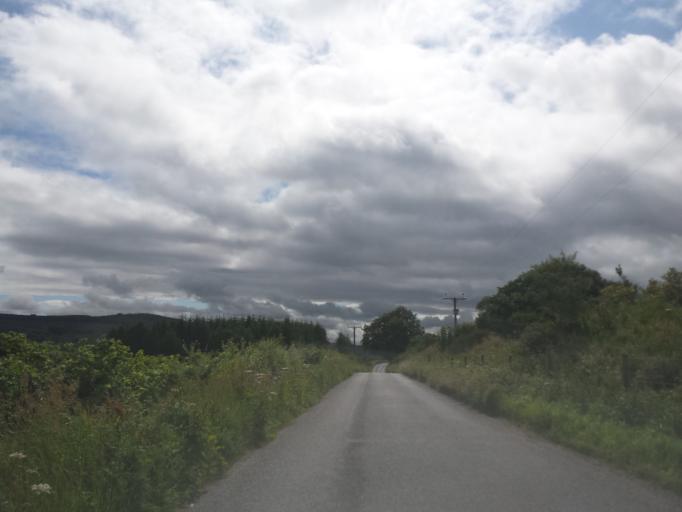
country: GB
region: Scotland
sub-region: Highland
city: Fortrose
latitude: 57.4742
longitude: -4.0882
